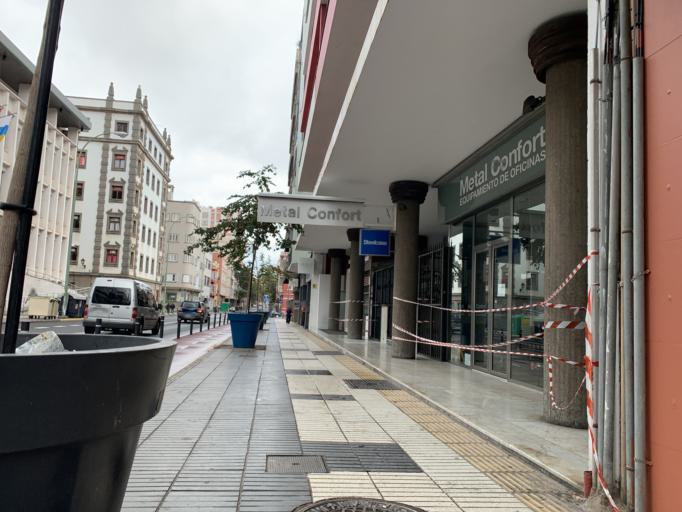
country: ES
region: Canary Islands
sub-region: Provincia de Las Palmas
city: Las Palmas de Gran Canaria
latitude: 28.1041
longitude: -15.4189
